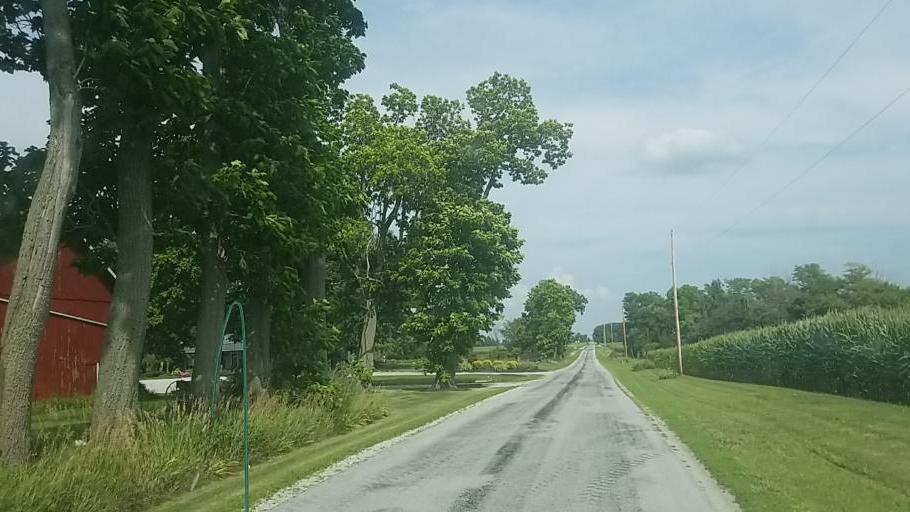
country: US
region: Ohio
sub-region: Hardin County
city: Forest
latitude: 40.8176
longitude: -83.4523
